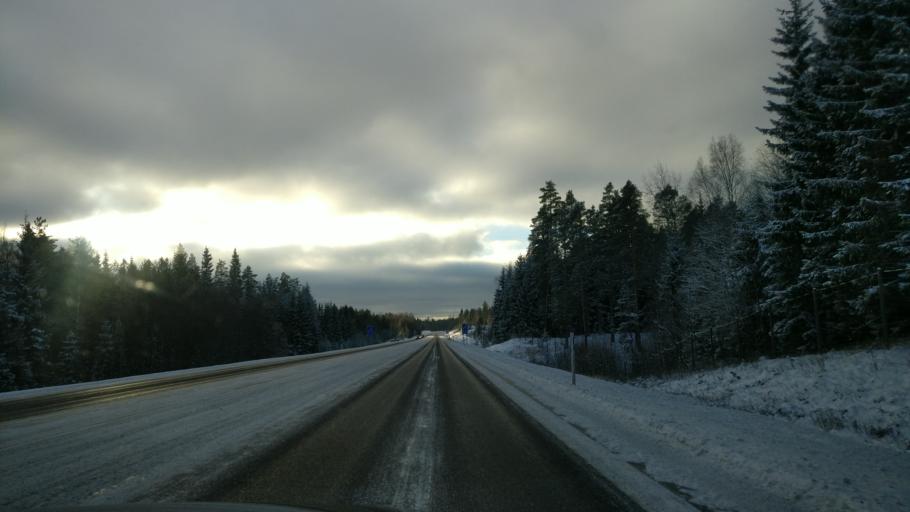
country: FI
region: Paijanne Tavastia
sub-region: Lahti
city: Heinola
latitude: 61.3564
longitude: 26.2304
